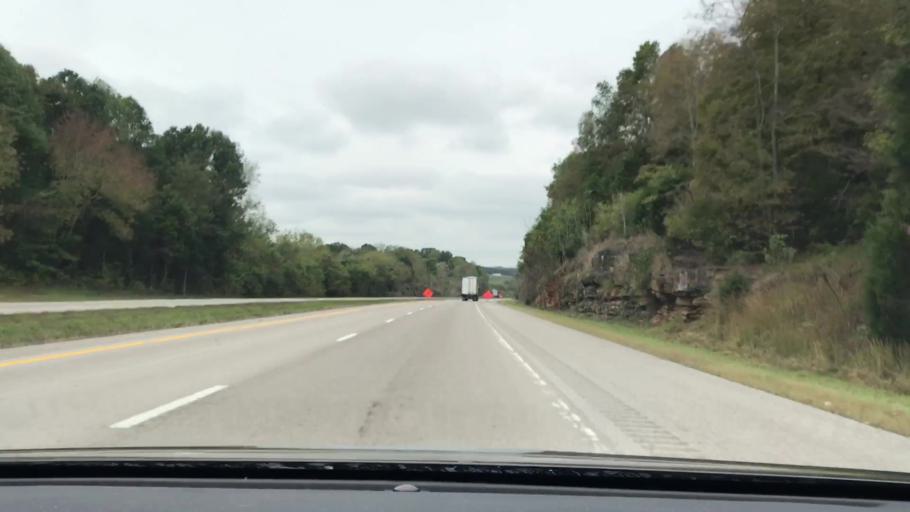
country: US
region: Kentucky
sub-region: Metcalfe County
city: Edmonton
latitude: 36.9974
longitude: -85.6315
